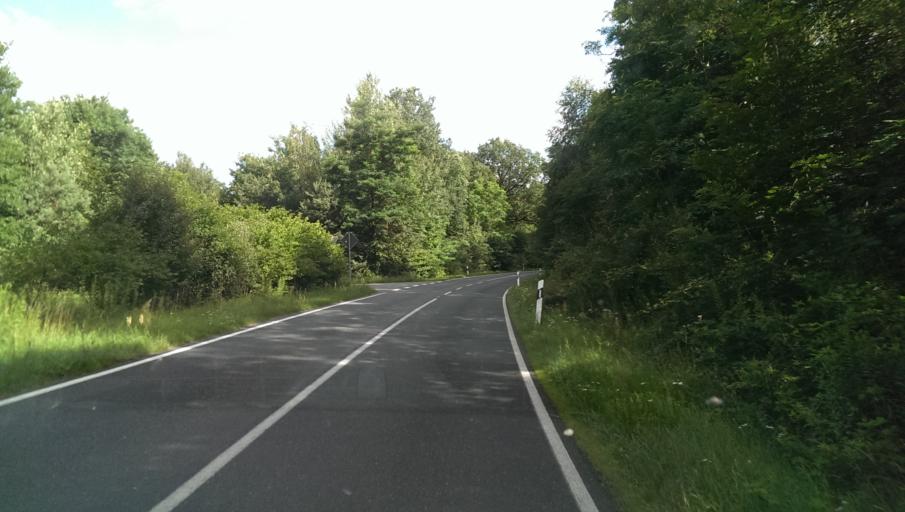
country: DE
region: Saxony-Anhalt
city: Radis
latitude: 51.7586
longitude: 12.5058
